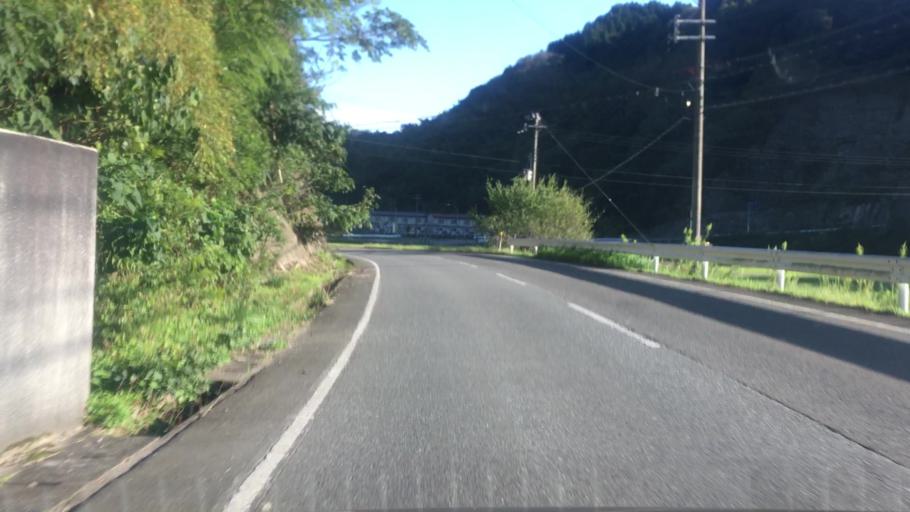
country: JP
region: Hyogo
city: Toyooka
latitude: 35.6073
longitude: 134.8071
